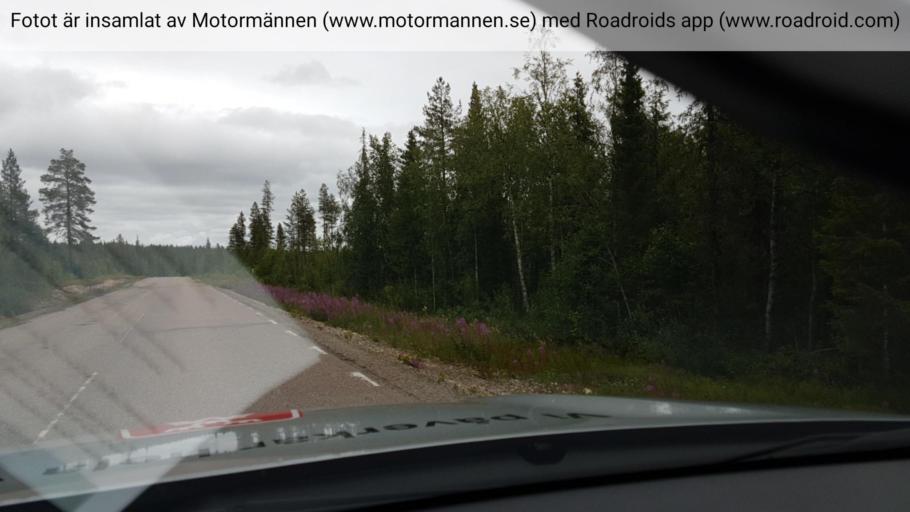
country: SE
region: Norrbotten
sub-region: Overkalix Kommun
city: OEverkalix
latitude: 67.0606
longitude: 22.2315
